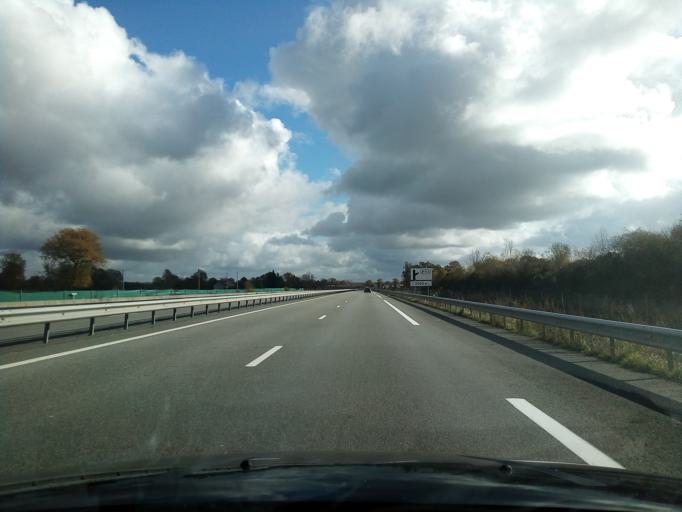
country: FR
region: Limousin
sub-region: Departement de la Creuse
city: Gouzon
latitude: 46.1974
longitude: 2.2086
